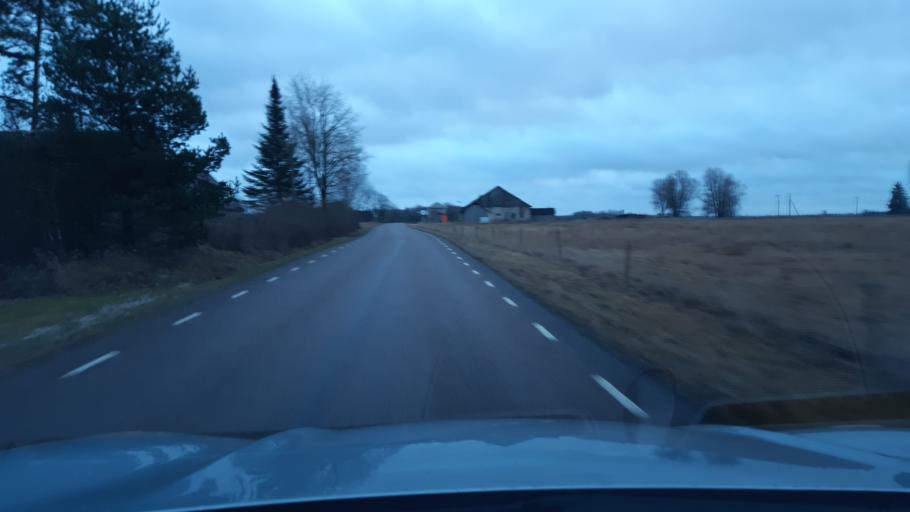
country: EE
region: Raplamaa
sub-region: Rapla vald
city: Rapla
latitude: 59.0168
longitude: 24.6986
